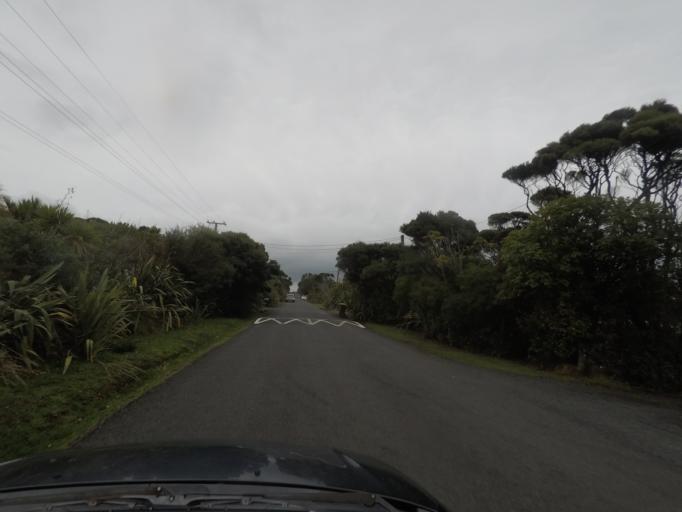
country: NZ
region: Auckland
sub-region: Auckland
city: Muriwai Beach
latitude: -36.9681
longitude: 174.4769
